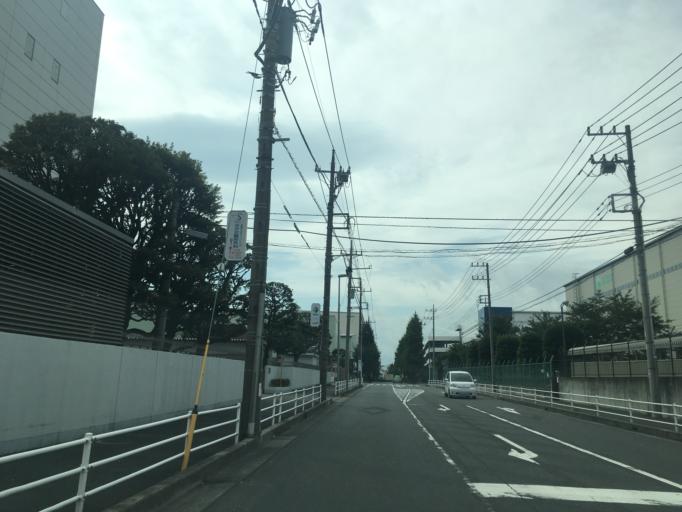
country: JP
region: Tokyo
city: Hachioji
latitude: 35.5888
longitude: 139.3511
